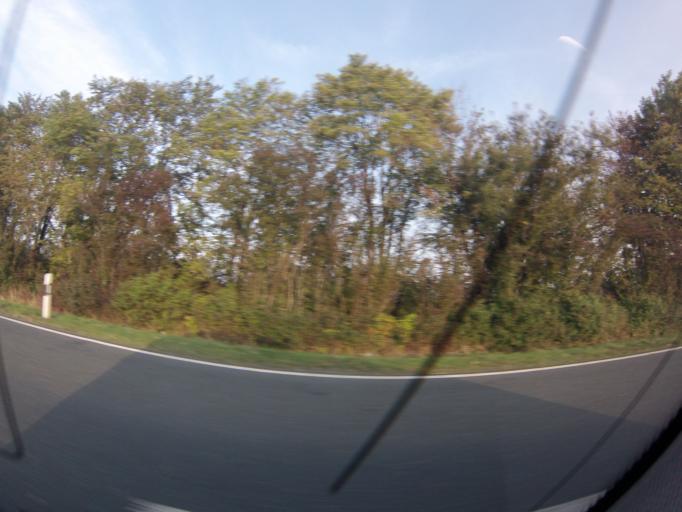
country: DE
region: Thuringia
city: Altkirchen
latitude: 50.9290
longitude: 12.3458
